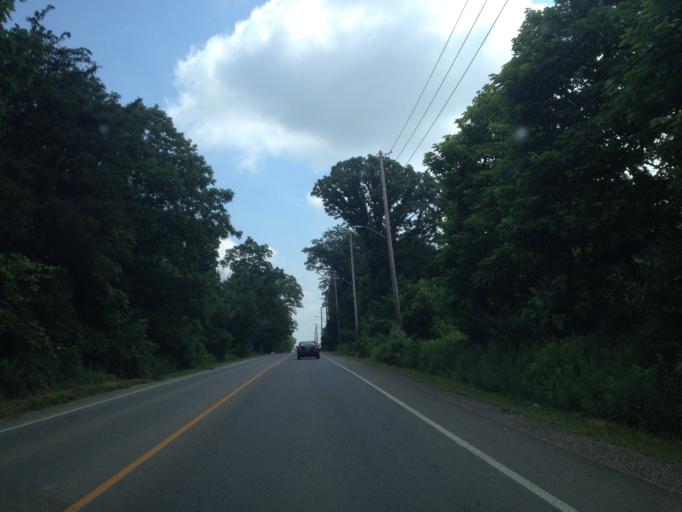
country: CA
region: Ontario
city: London
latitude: 43.0291
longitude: -81.1833
